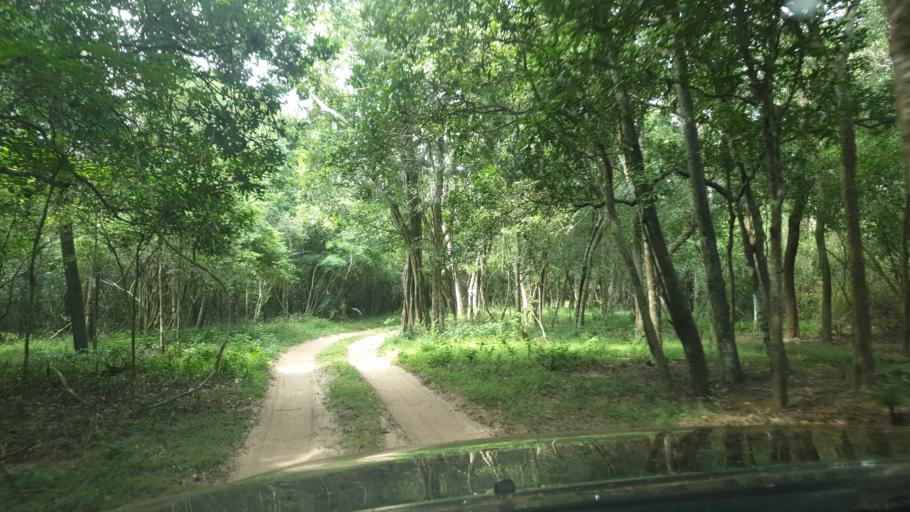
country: LK
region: North Western
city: Puttalam
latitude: 8.4125
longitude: 79.9840
